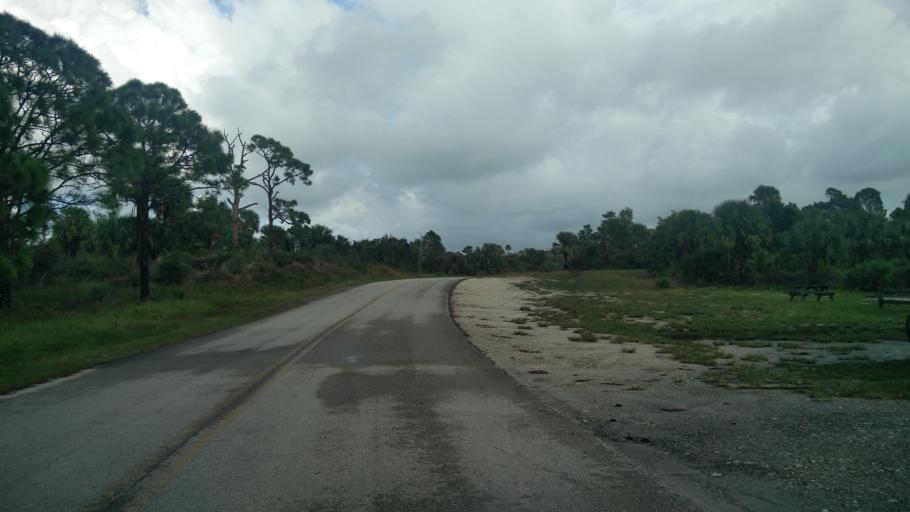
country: US
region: Florida
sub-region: Palm Beach County
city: Tequesta
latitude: 27.0120
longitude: -80.1122
